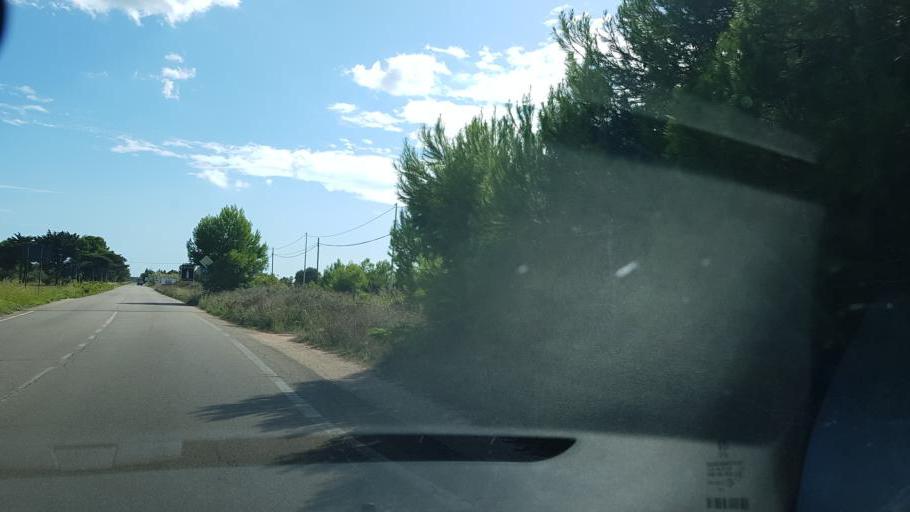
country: IT
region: Apulia
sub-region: Provincia di Lecce
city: Borgagne
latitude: 40.2655
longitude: 18.4318
